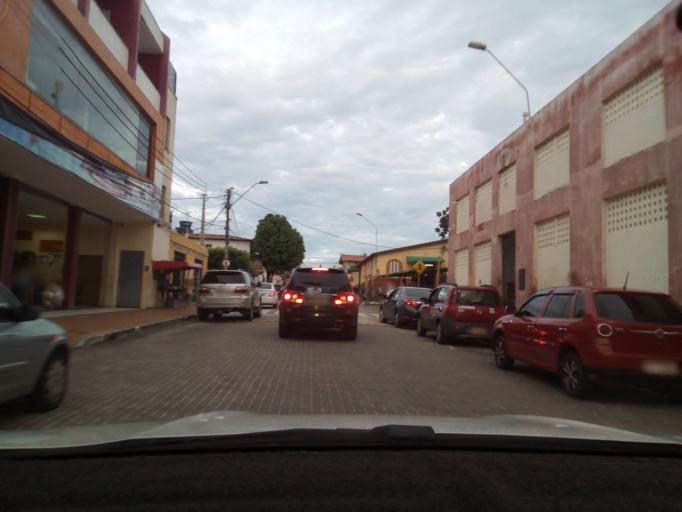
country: BR
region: Ceara
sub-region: Beberibe
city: Beberibe
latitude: -4.1812
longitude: -38.1301
